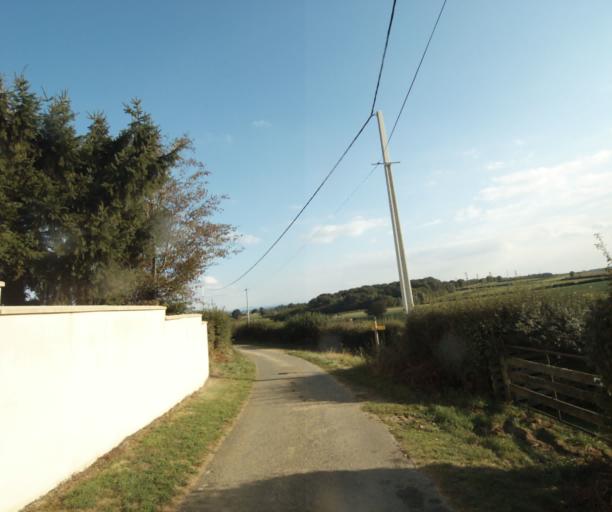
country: FR
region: Bourgogne
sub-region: Departement de Saone-et-Loire
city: Gueugnon
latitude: 46.5841
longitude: 4.1335
